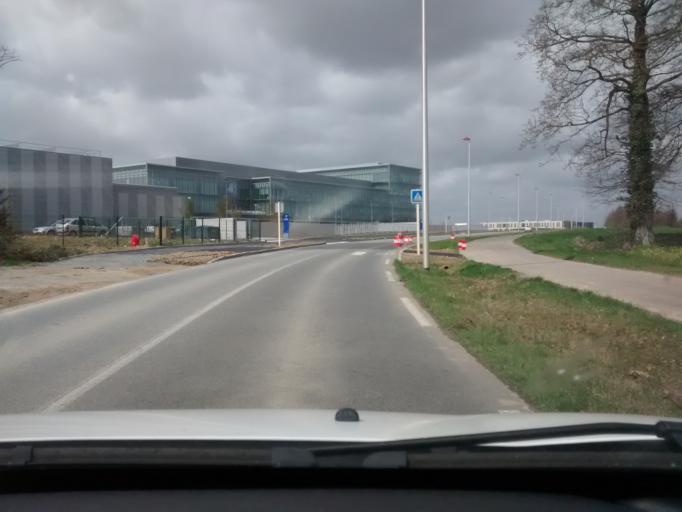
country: FR
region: Brittany
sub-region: Departement d'Ille-et-Vilaine
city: Saint-Gregoire
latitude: 48.1457
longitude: -1.6954
